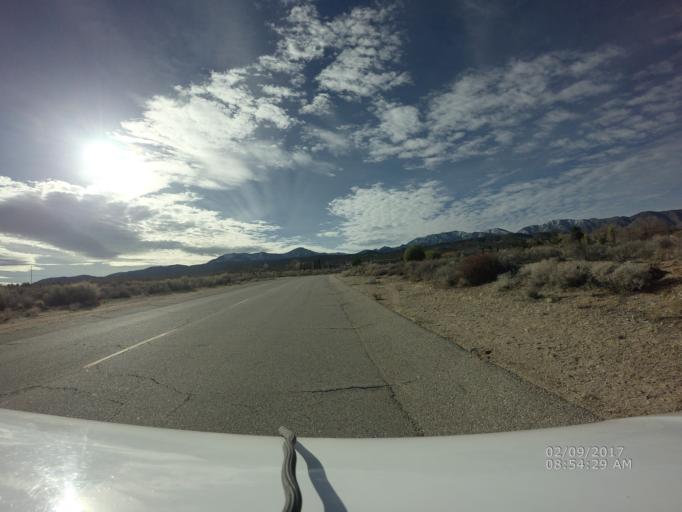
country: US
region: California
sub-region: Los Angeles County
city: Lake Los Angeles
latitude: 34.4760
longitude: -117.8369
